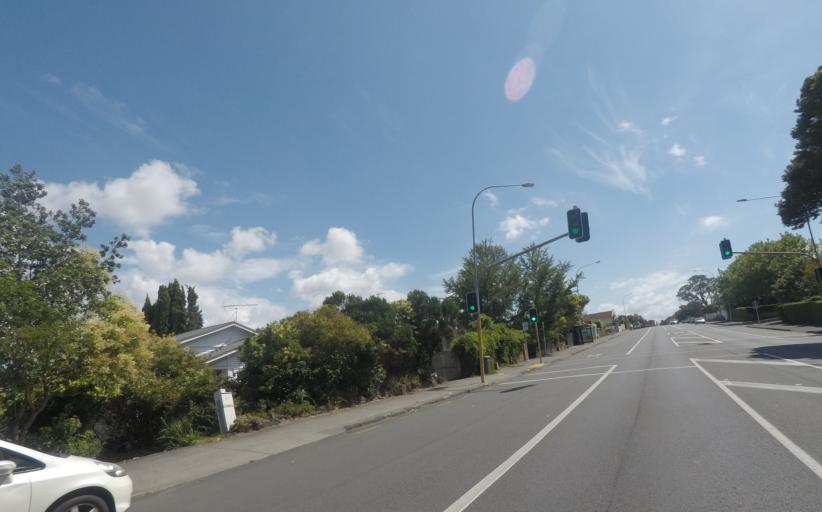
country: NZ
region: Auckland
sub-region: Auckland
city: Tamaki
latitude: -36.8797
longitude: 174.8177
